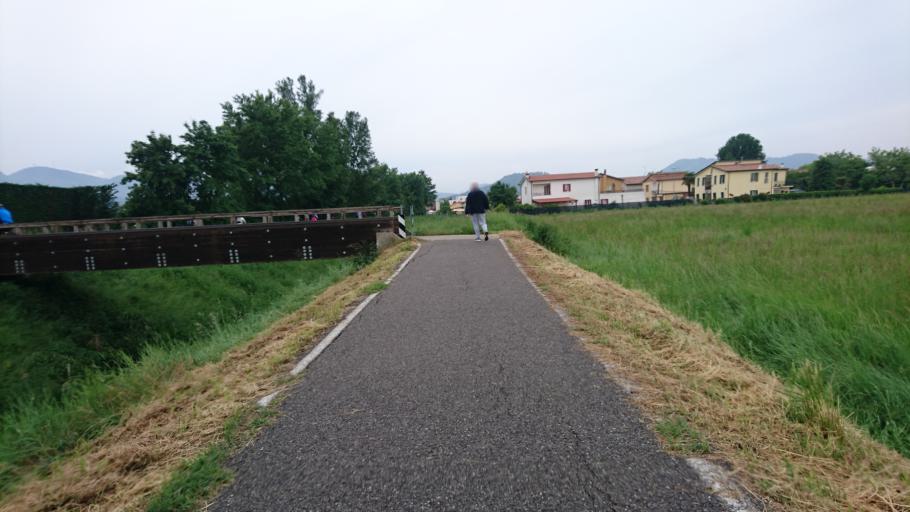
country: IT
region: Veneto
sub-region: Provincia di Padova
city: Montegrotto Terme
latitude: 45.3396
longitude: 11.7639
